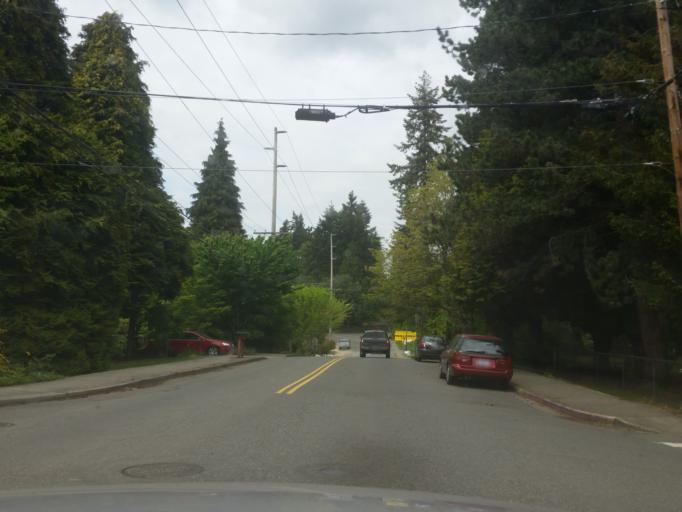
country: US
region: Washington
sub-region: King County
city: Kirkland
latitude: 47.6856
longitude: -122.1972
